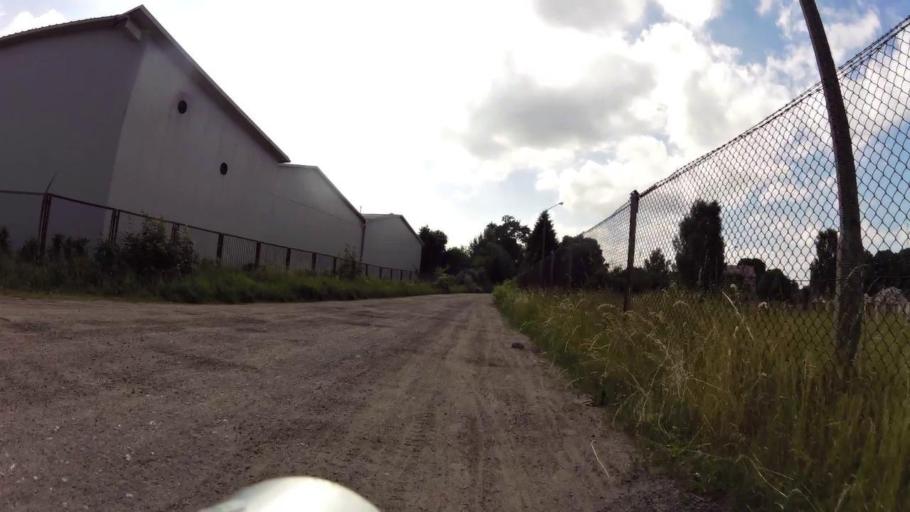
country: PL
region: West Pomeranian Voivodeship
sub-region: Powiat koszalinski
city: Bobolice
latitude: 53.9542
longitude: 16.5974
